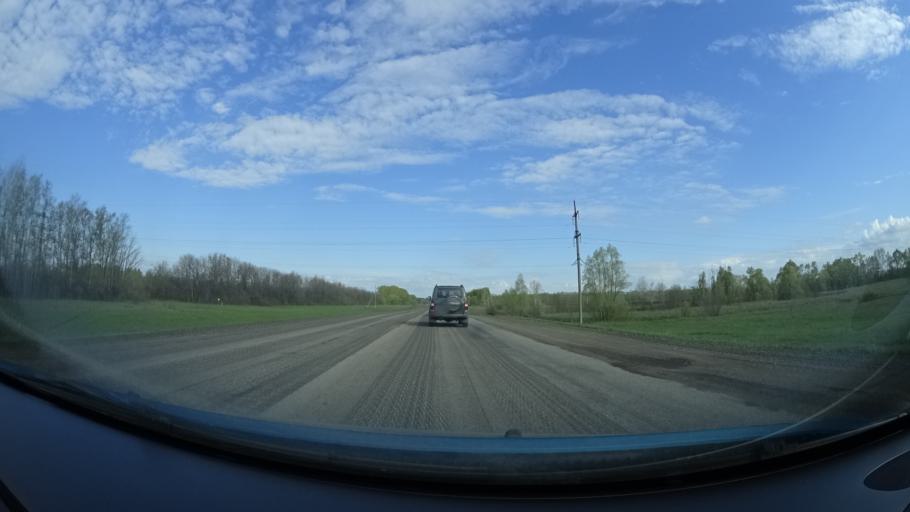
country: RU
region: Bashkortostan
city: Birsk
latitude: 55.2427
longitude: 55.7666
